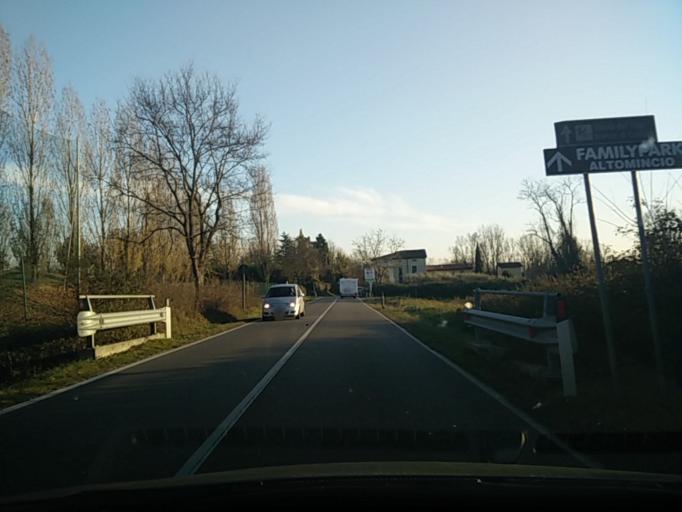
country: IT
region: Lombardy
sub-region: Provincia di Mantova
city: Ponti sul Mincio
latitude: 45.4262
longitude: 10.7037
